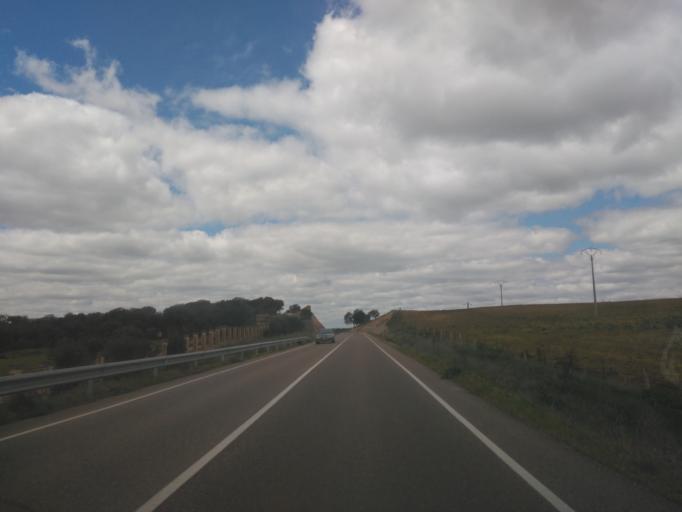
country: ES
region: Castille and Leon
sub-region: Provincia de Salamanca
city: Florida de Liebana
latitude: 41.0339
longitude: -5.7333
